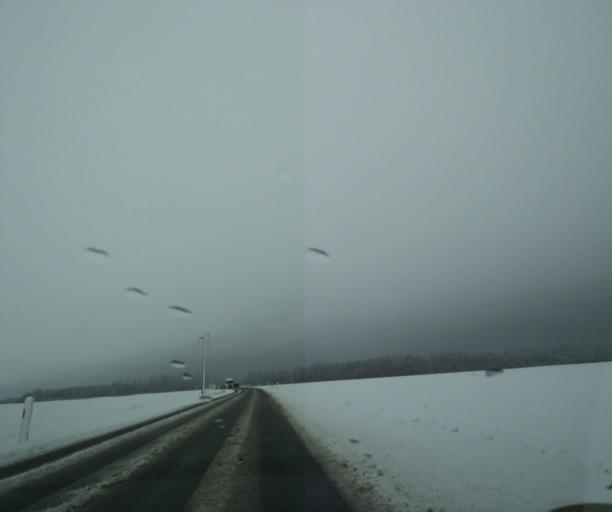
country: FR
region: Champagne-Ardenne
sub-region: Departement de la Haute-Marne
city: Wassy
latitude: 48.5531
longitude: 4.9258
